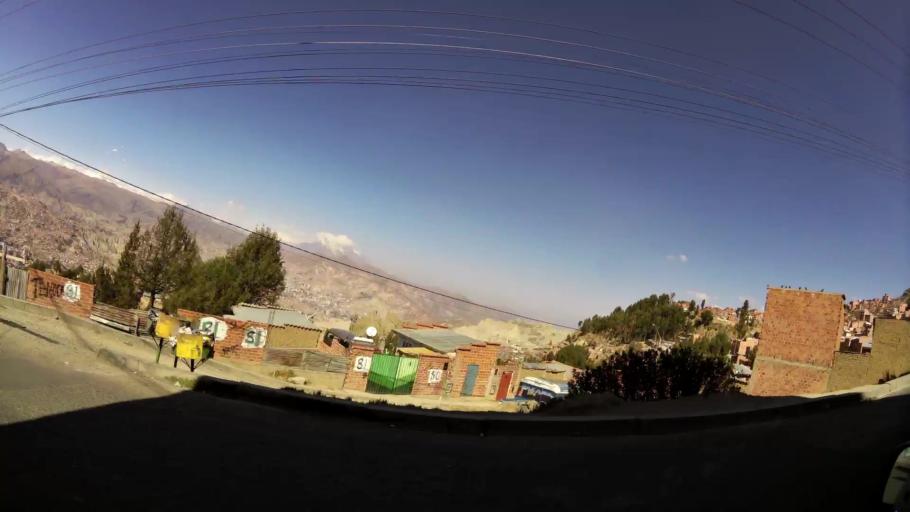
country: BO
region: La Paz
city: La Paz
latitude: -16.5218
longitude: -68.1426
